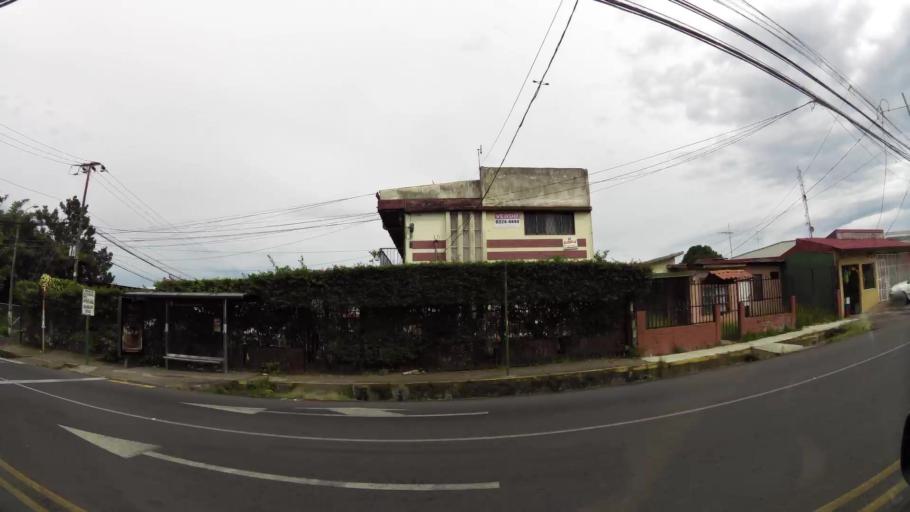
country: CR
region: San Jose
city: San Vicente de Moravia
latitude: 9.9631
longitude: -84.0534
